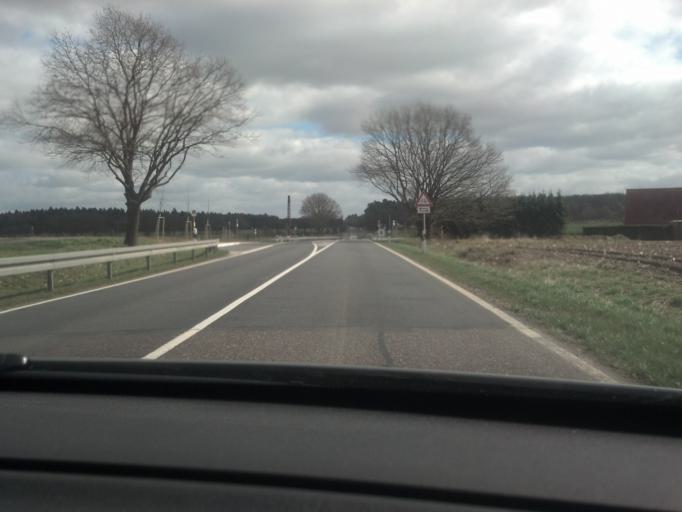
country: DE
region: Mecklenburg-Vorpommern
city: Malchow
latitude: 53.3645
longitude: 12.4316
